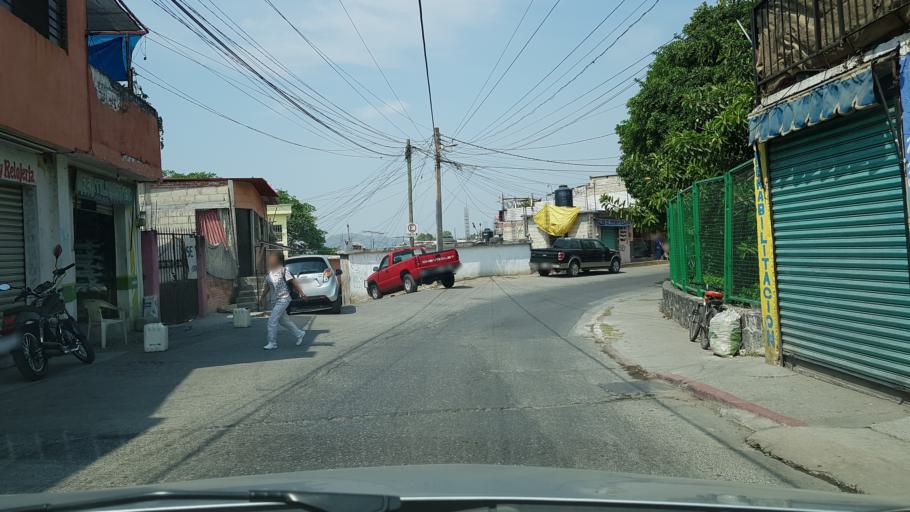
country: MX
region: Morelos
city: Emiliano Zapata
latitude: 18.8380
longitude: -99.1848
